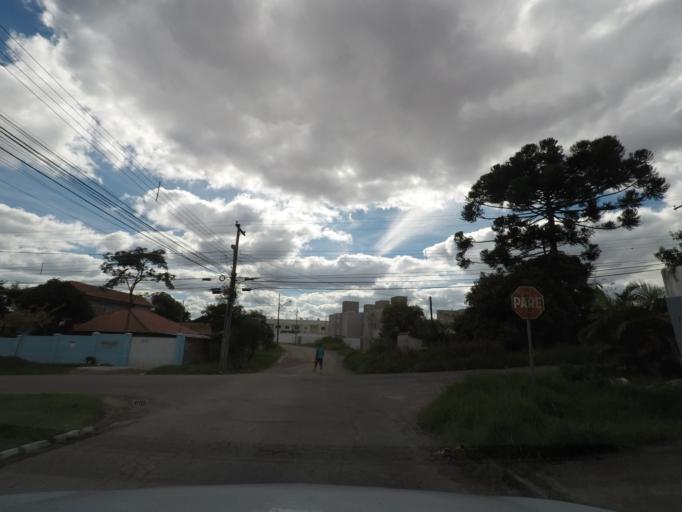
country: BR
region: Parana
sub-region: Pinhais
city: Pinhais
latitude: -25.4804
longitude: -49.2370
